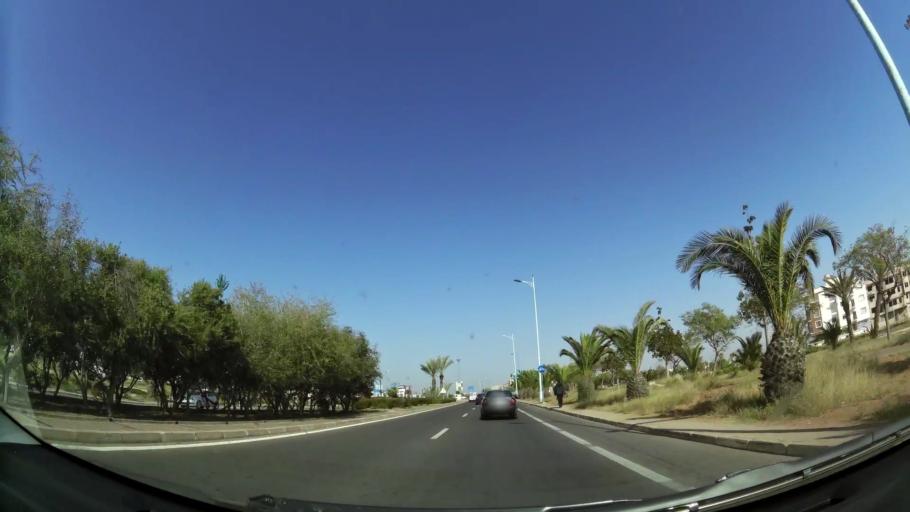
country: MA
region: Oued ed Dahab-Lagouira
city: Dakhla
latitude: 30.4045
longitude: -9.5346
